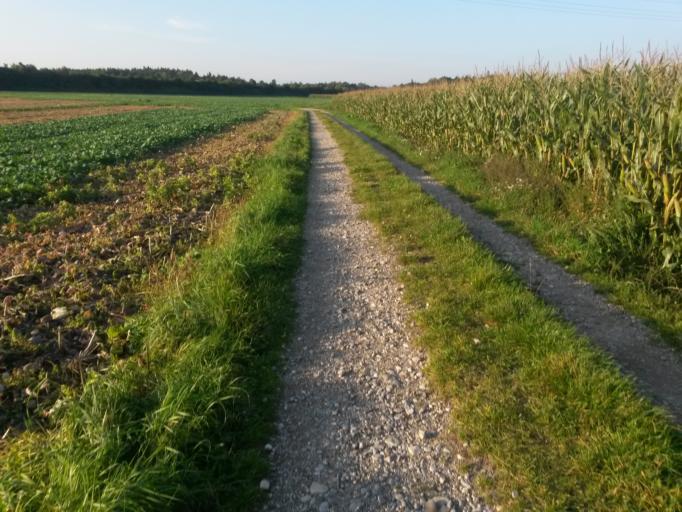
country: DE
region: Bavaria
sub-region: Upper Bavaria
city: Grasbrunn
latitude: 48.0844
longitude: 11.7439
